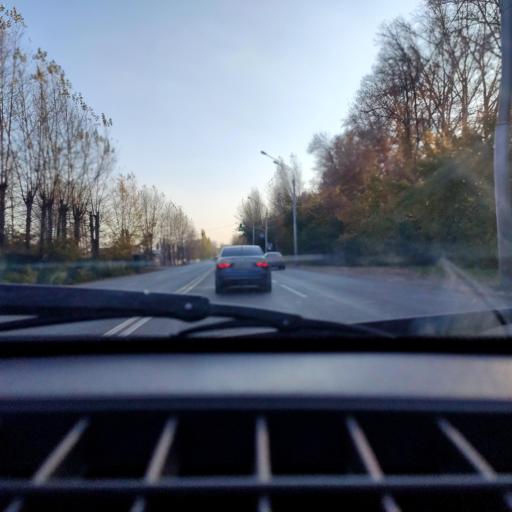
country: RU
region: Bashkortostan
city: Avdon
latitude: 54.6907
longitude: 55.8180
